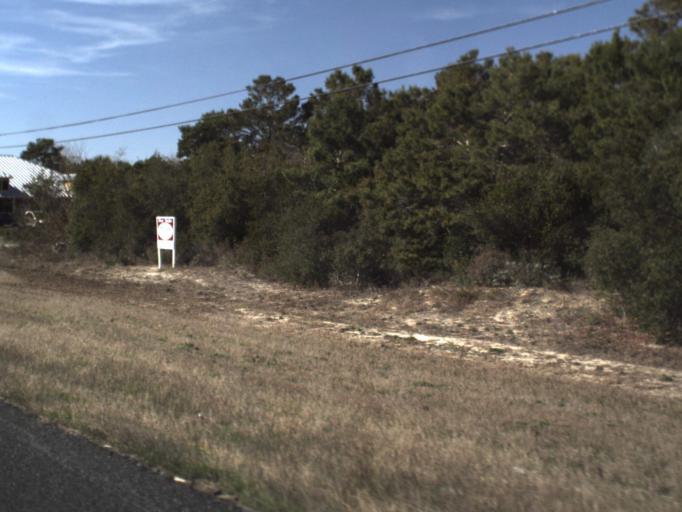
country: US
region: Florida
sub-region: Bay County
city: Laguna Beach
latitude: 30.2631
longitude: -85.9648
